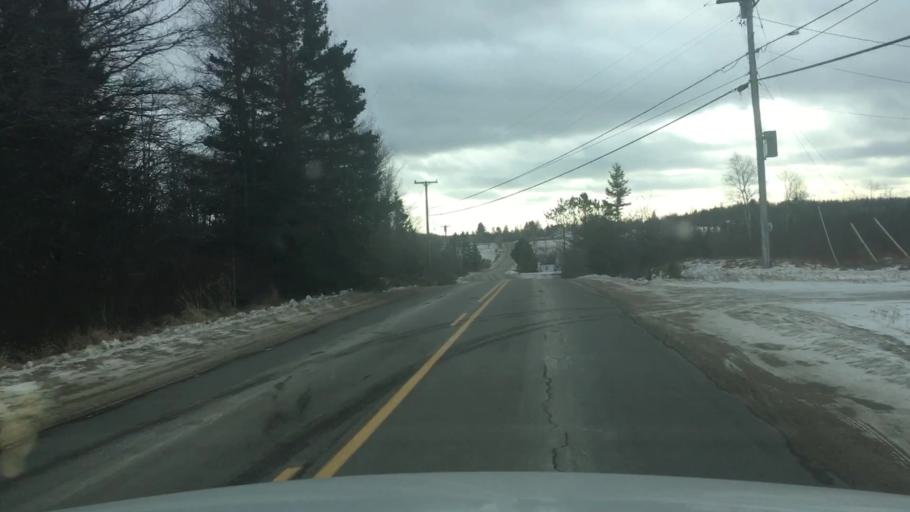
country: US
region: Maine
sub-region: Washington County
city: Machias
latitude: 44.6805
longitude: -67.4675
